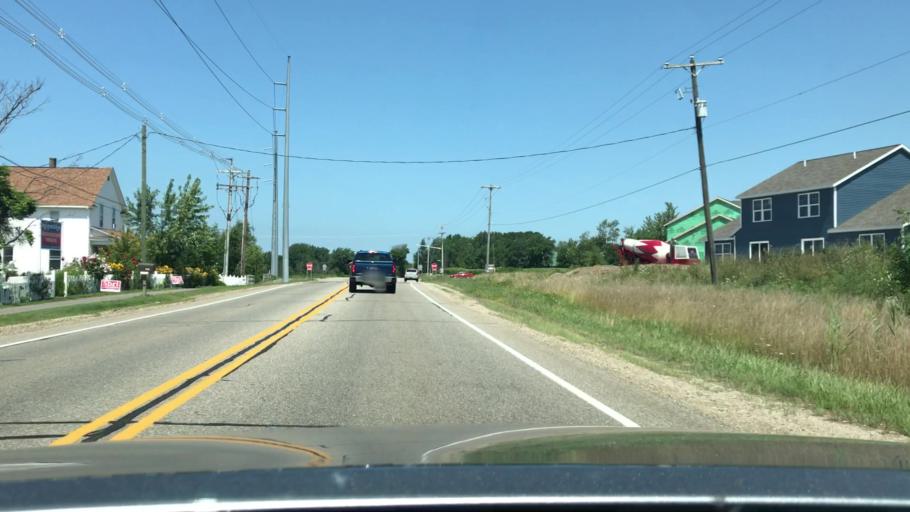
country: US
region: Michigan
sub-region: Ottawa County
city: Holland
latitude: 42.8400
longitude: -86.0789
